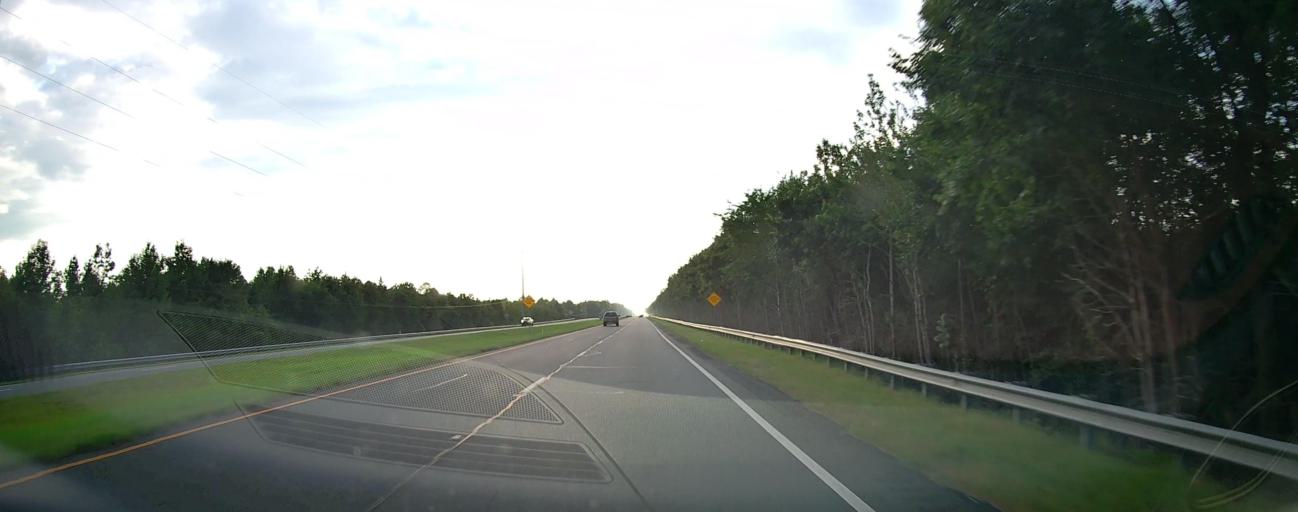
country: US
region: Georgia
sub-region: Taylor County
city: Reynolds
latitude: 32.5414
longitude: -84.0268
